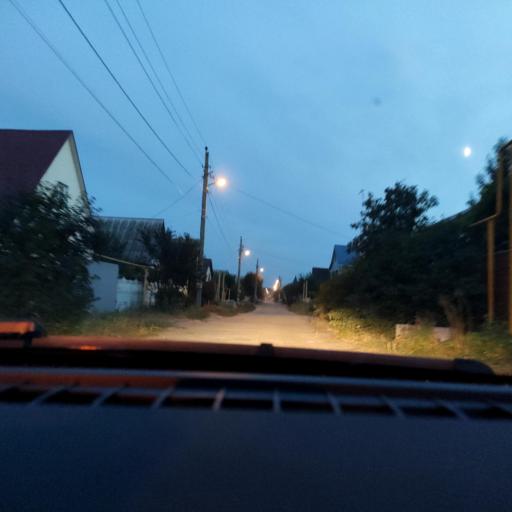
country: RU
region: Voronezj
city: Maslovka
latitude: 51.5457
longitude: 39.2419
